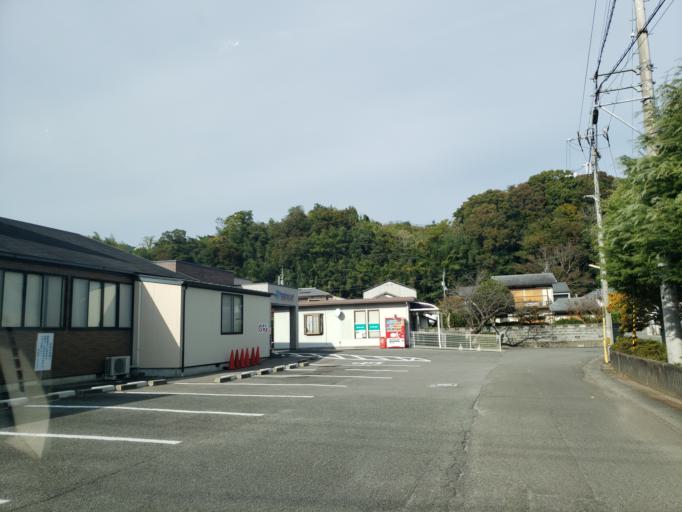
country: JP
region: Tokushima
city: Wakimachi
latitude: 34.0674
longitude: 134.1549
